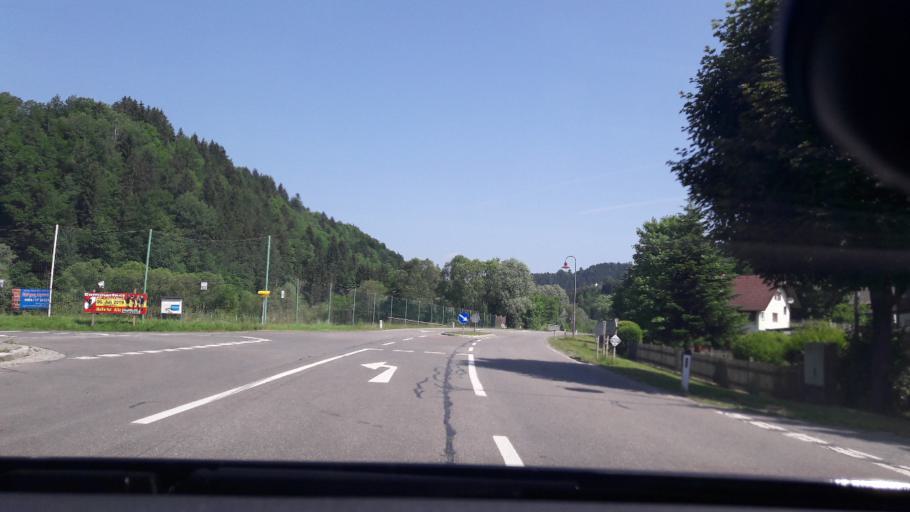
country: AT
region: Styria
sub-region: Politischer Bezirk Voitsberg
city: Sodingberg
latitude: 47.1082
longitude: 15.1723
